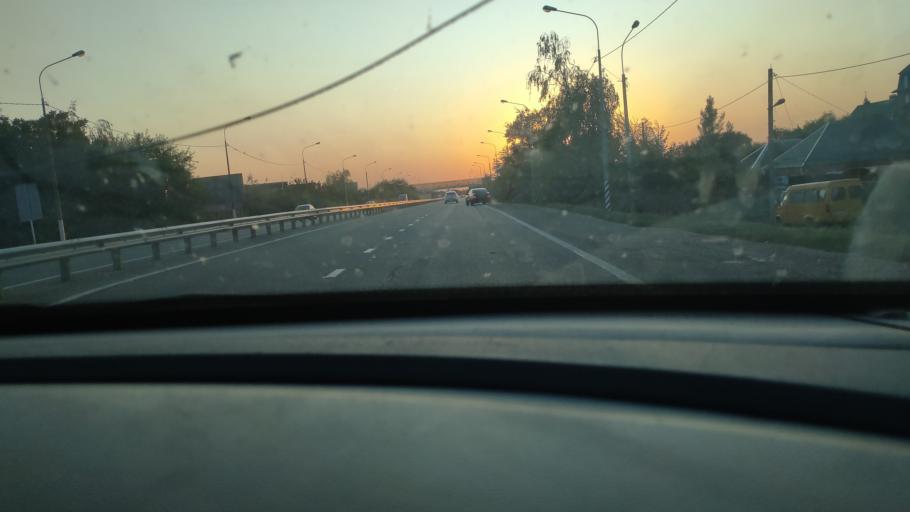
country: RU
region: Krasnodarskiy
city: Timashevsk
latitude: 45.6001
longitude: 38.9552
